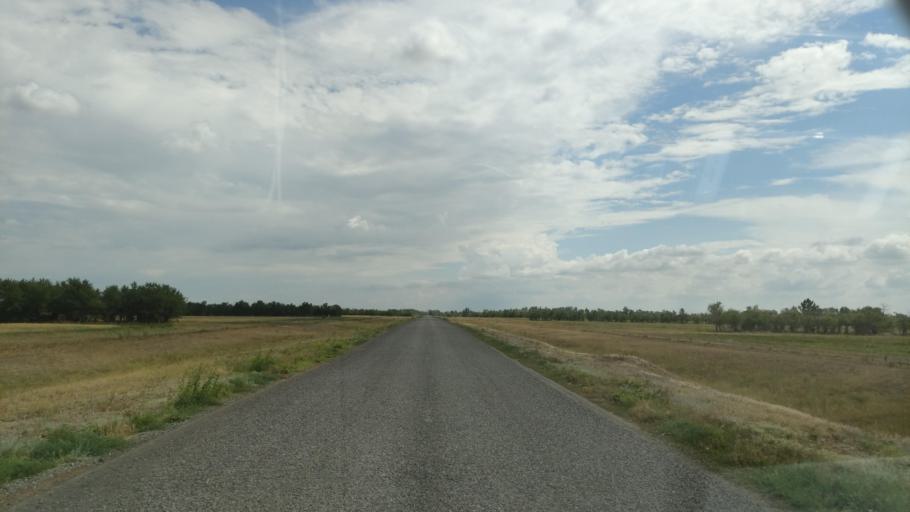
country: KZ
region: Pavlodar
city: Pavlodar
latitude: 52.6367
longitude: 76.9754
